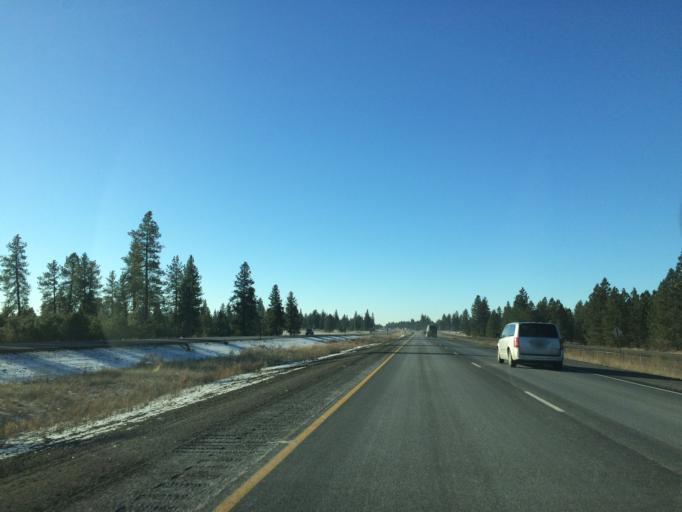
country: US
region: Washington
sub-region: Spokane County
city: Medical Lake
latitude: 47.4434
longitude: -117.7806
